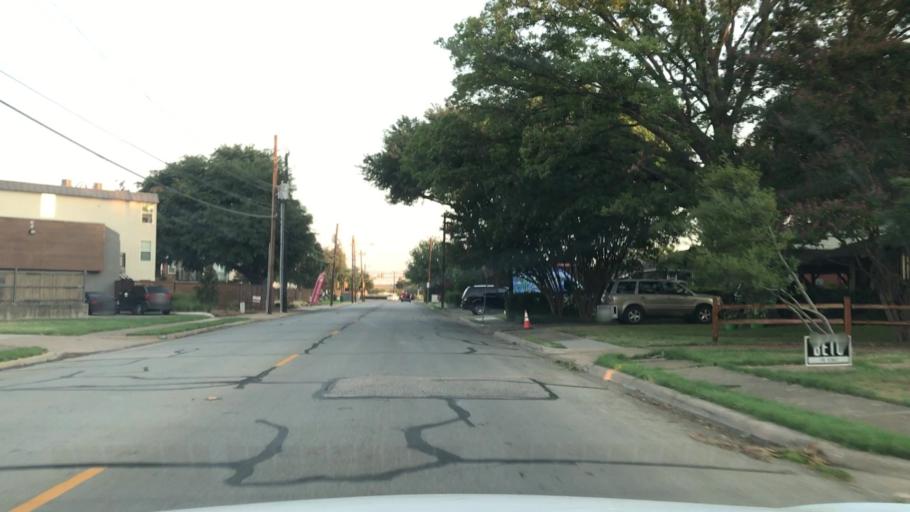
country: US
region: Texas
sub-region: Dallas County
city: Highland Park
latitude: 32.8537
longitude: -96.7501
